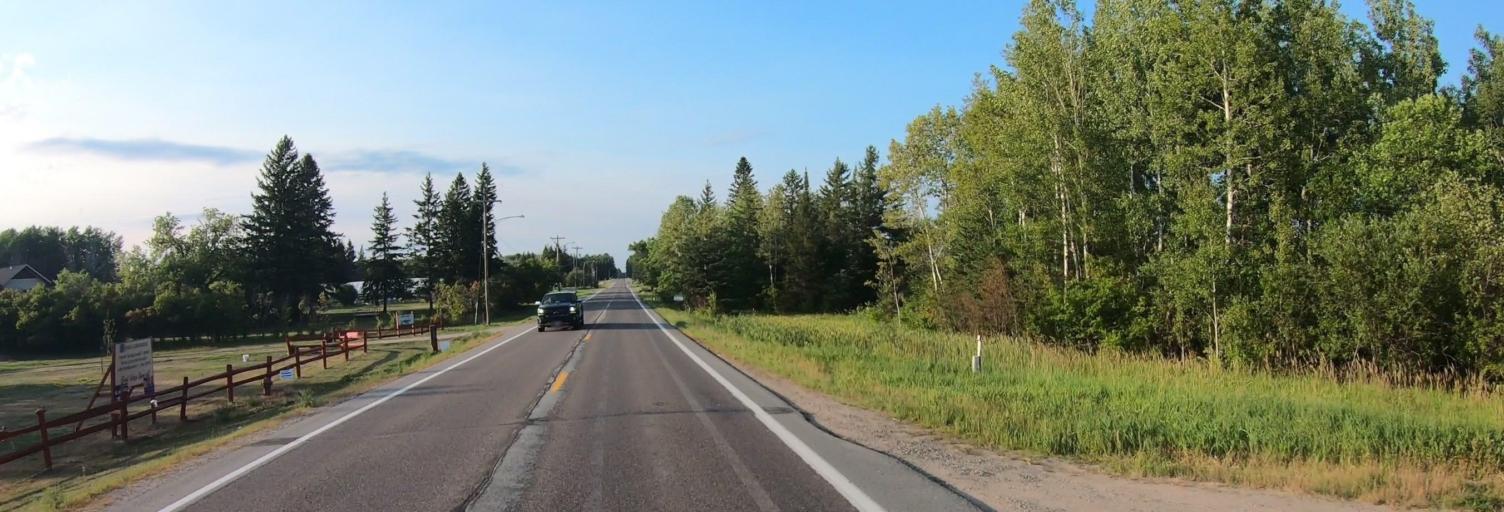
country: US
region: Minnesota
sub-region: Saint Louis County
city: Mountain Iron
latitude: 47.8568
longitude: -92.6839
